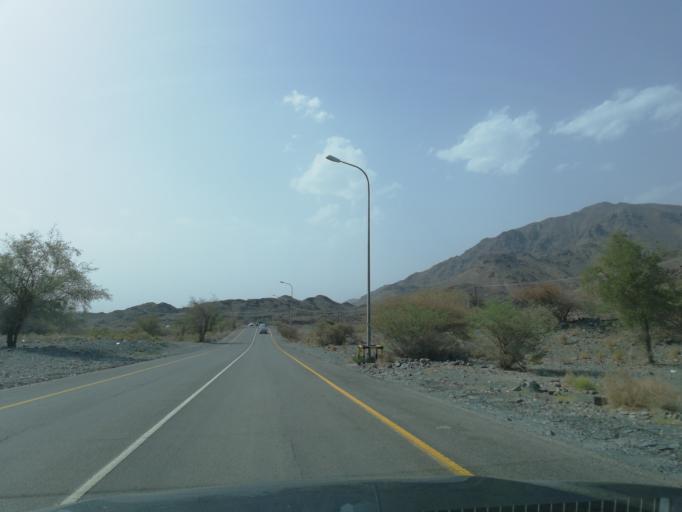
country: OM
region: Muhafazat ad Dakhiliyah
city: Sufalat Sama'il
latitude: 23.1558
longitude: 58.1139
